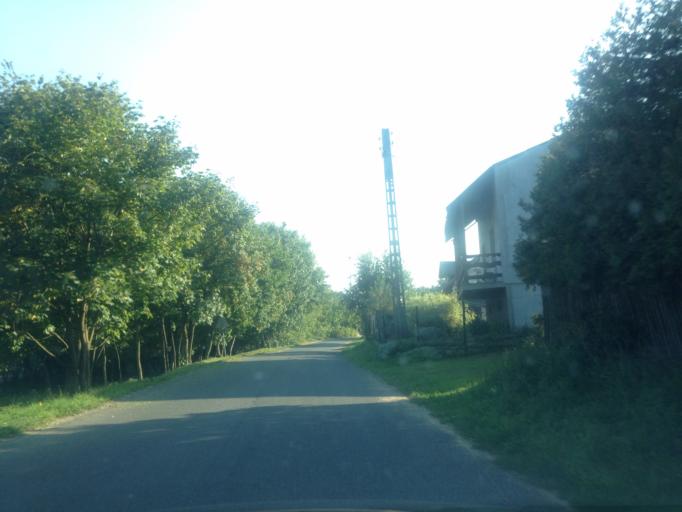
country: PL
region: Kujawsko-Pomorskie
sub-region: Powiat brodnicki
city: Brzozie
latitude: 53.2916
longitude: 19.6919
